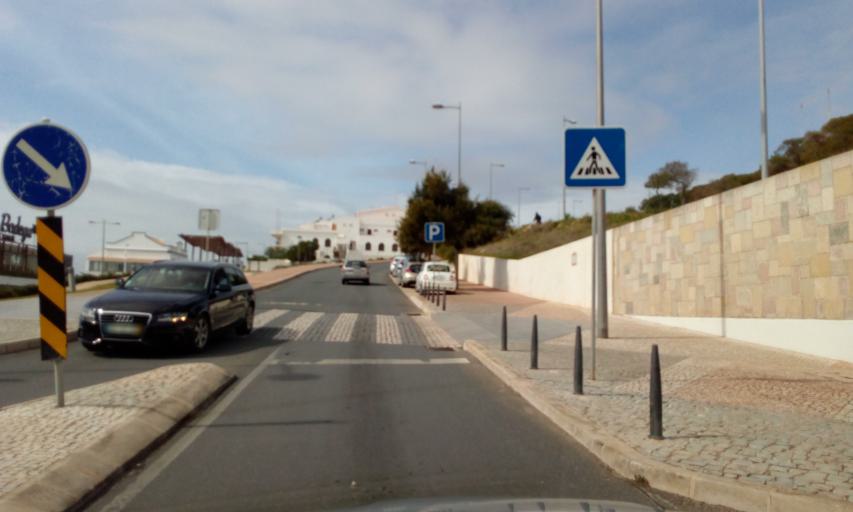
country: PT
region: Faro
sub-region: Albufeira
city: Albufeira
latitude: 37.0864
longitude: -8.2440
